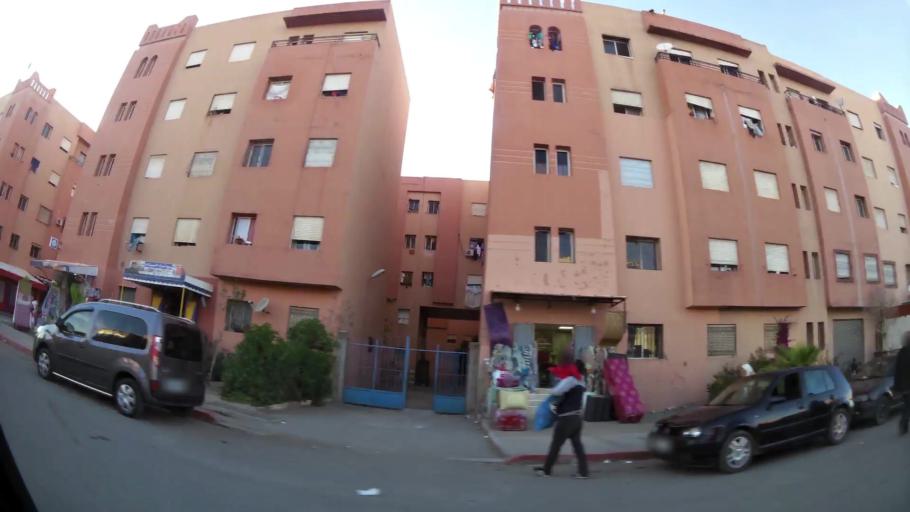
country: MA
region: Marrakech-Tensift-Al Haouz
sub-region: Marrakech
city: Marrakesh
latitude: 31.7478
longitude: -8.1187
